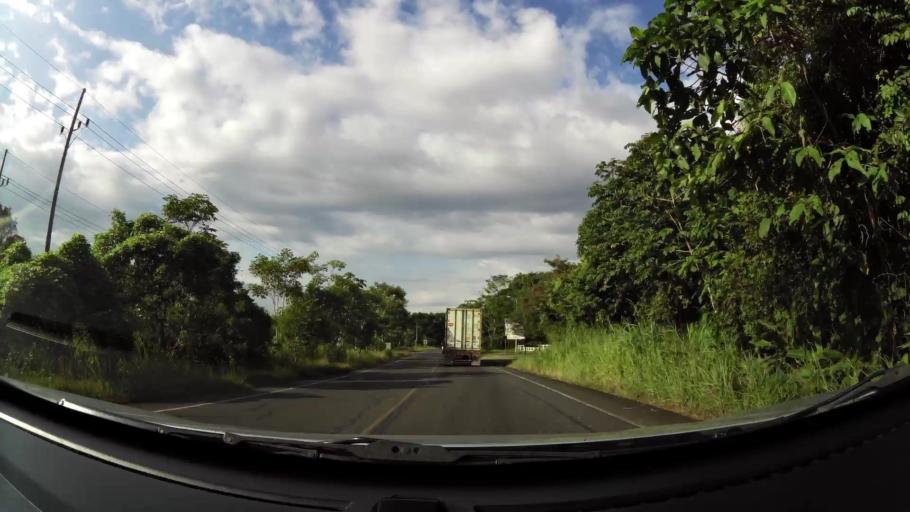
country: CR
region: Alajuela
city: Orotina
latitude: 9.7802
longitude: -84.6068
